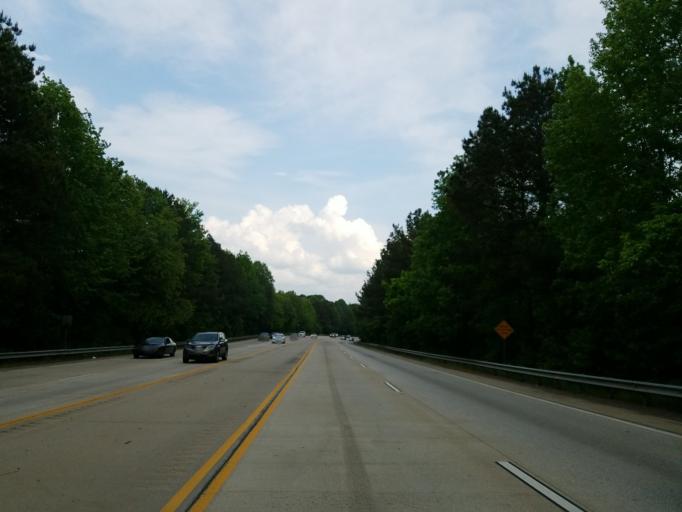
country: US
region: Georgia
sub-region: Cobb County
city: Powder Springs
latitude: 33.8310
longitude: -84.6725
